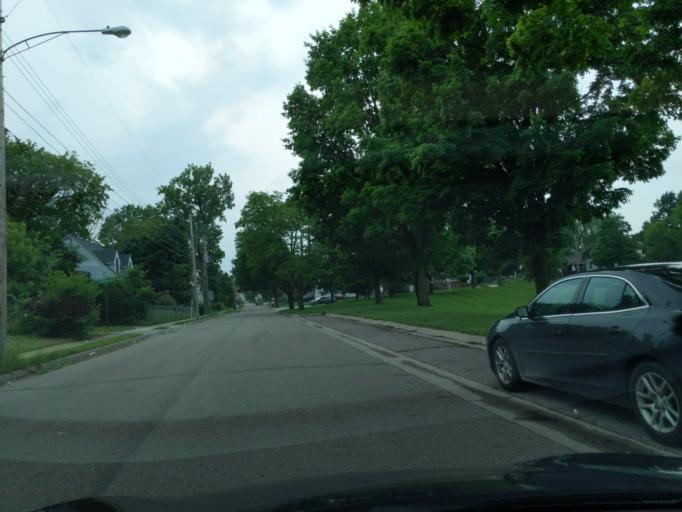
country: US
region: Michigan
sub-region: Ingham County
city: Lansing
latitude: 42.7446
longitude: -84.5647
